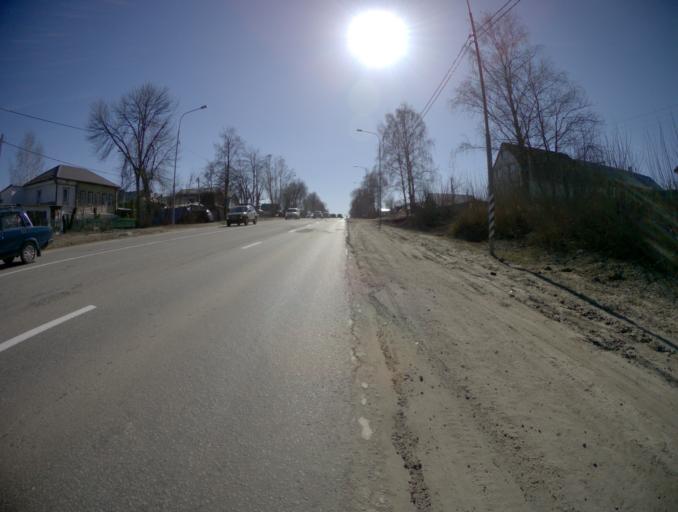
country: RU
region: Vladimir
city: Bogolyubovo
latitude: 56.1896
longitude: 40.5230
